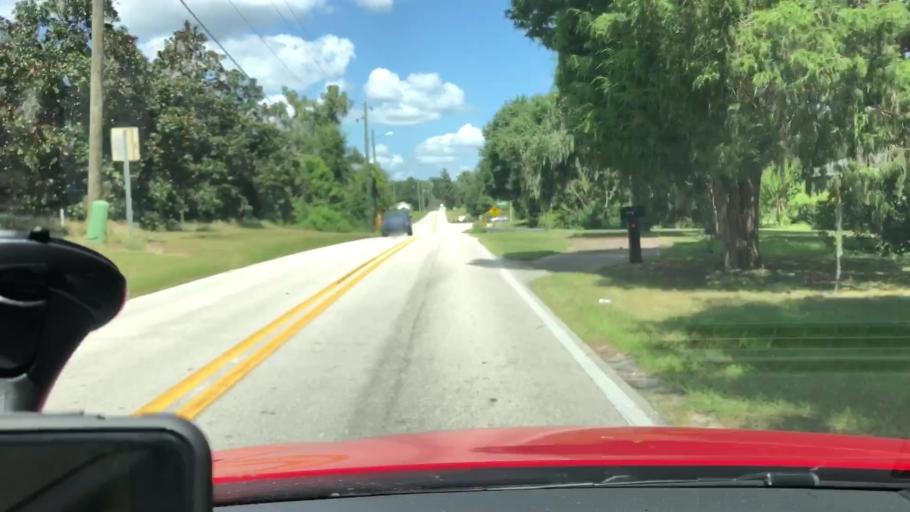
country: US
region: Florida
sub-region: Volusia County
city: North DeLand
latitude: 29.0530
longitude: -81.3166
